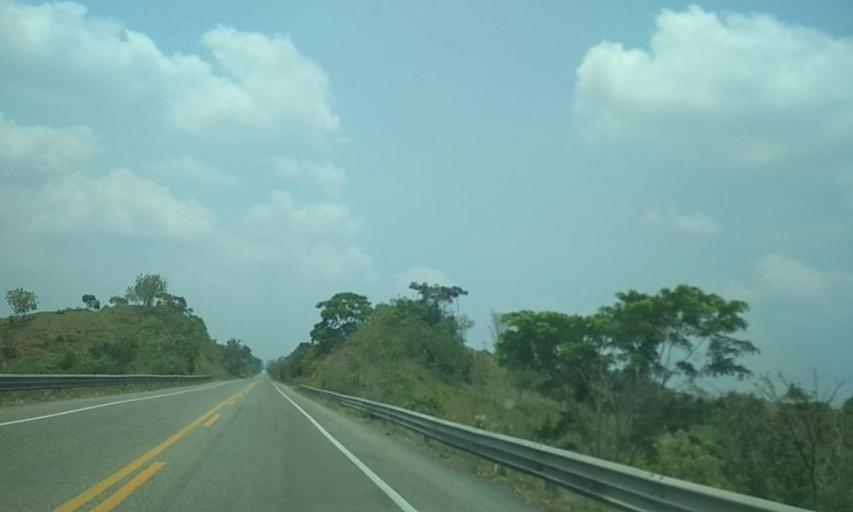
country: MX
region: Tabasco
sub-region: Huimanguillo
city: Francisco Rueda
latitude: 17.6587
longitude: -93.8505
